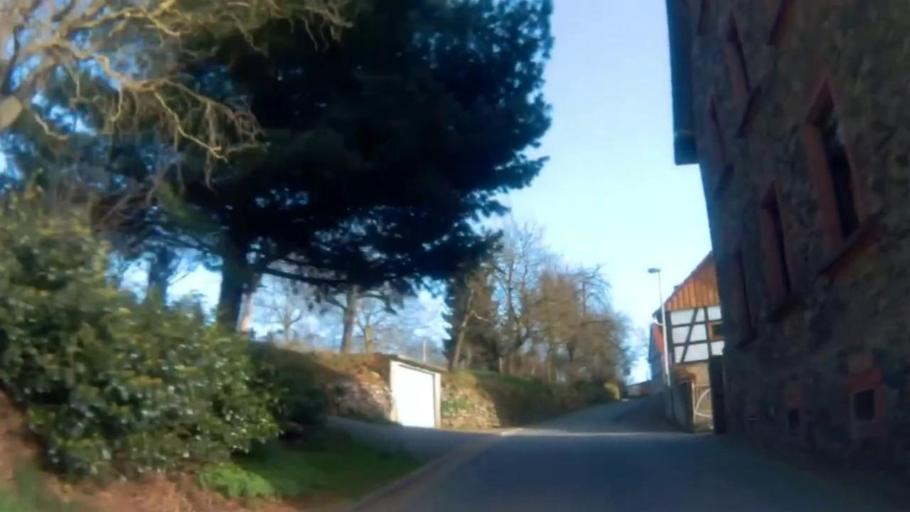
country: DE
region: Hesse
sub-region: Regierungsbezirk Darmstadt
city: Frankisch-Crumbach
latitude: 49.7529
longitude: 8.8241
